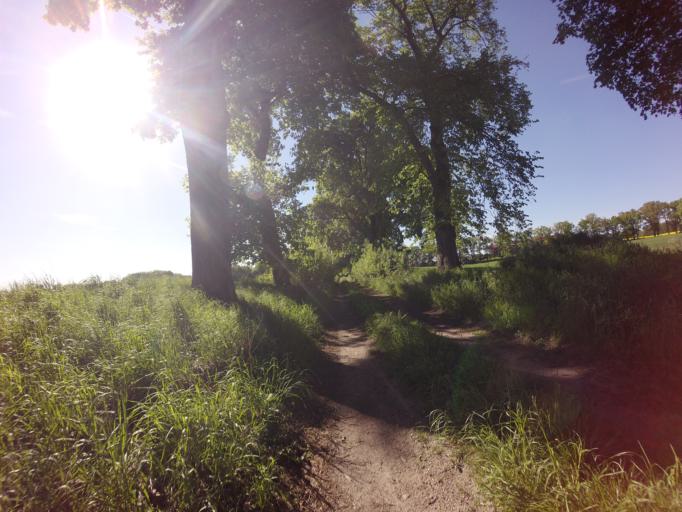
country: PL
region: West Pomeranian Voivodeship
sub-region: Powiat stargardzki
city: Dolice
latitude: 53.1591
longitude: 15.2908
